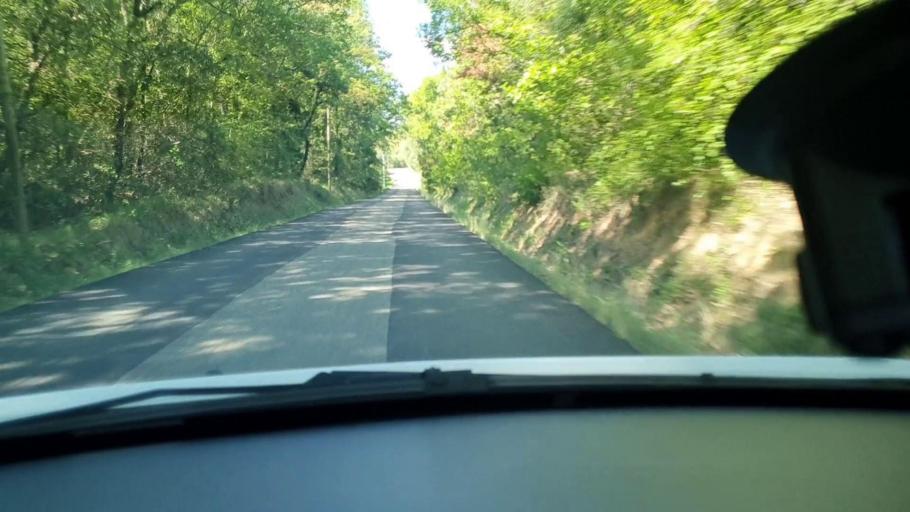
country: FR
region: Languedoc-Roussillon
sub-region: Departement du Gard
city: Goudargues
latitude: 44.1757
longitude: 4.5008
